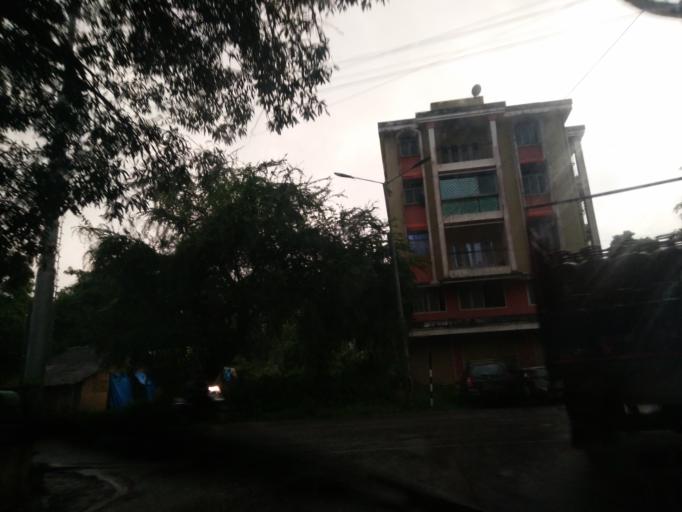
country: IN
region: Goa
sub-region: South Goa
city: Madgaon
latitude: 15.2833
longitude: 73.9664
